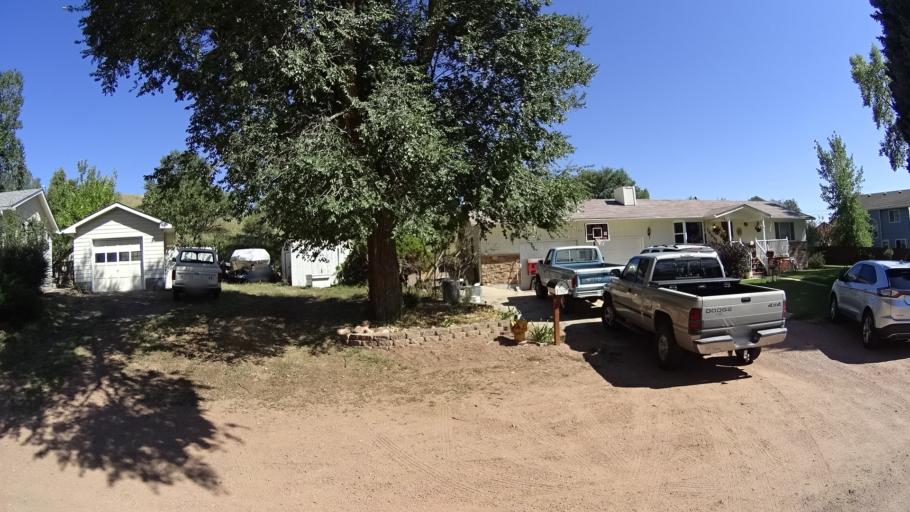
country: US
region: Colorado
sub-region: El Paso County
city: Colorado Springs
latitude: 38.8546
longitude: -104.8468
